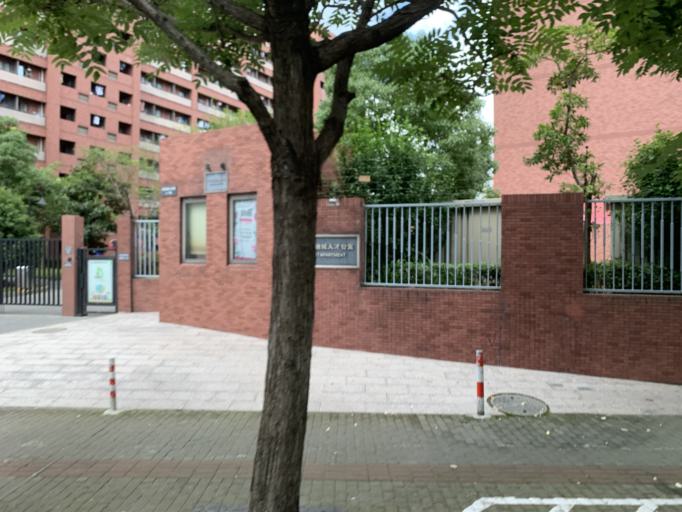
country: CN
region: Shanghai Shi
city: Huamu
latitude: 31.2038
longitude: 121.5290
